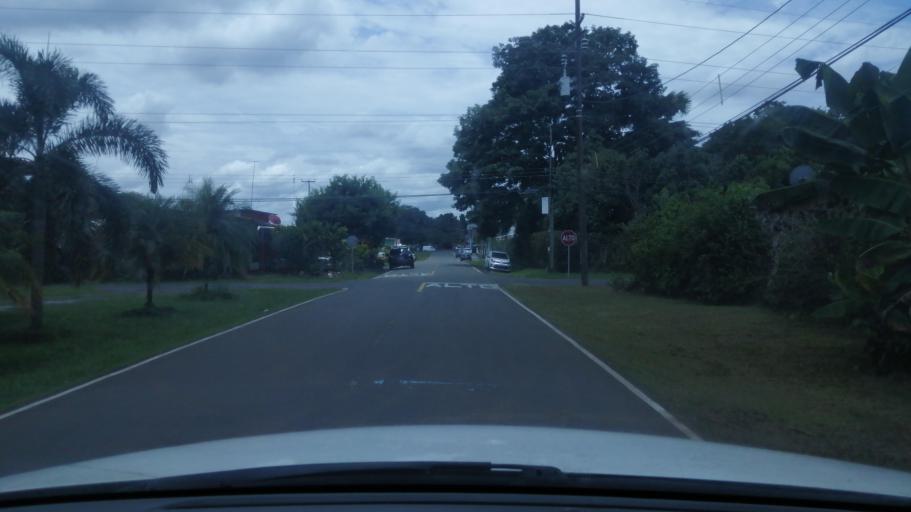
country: PA
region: Chiriqui
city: David
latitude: 8.4494
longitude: -82.4237
